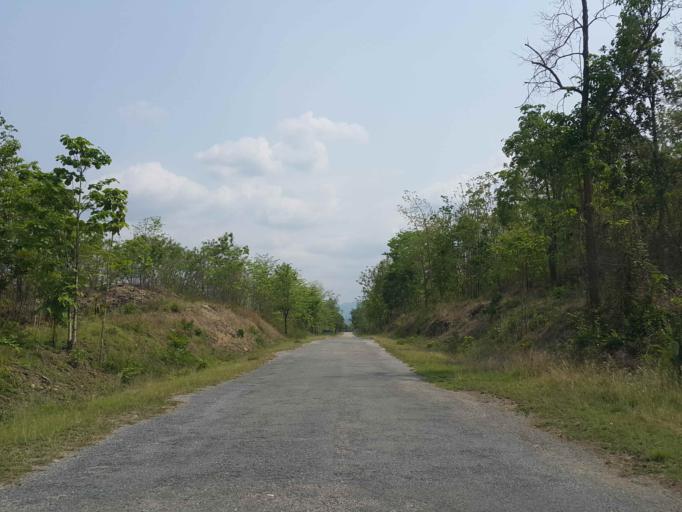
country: TH
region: Sukhothai
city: Thung Saliam
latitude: 17.3327
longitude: 99.4238
